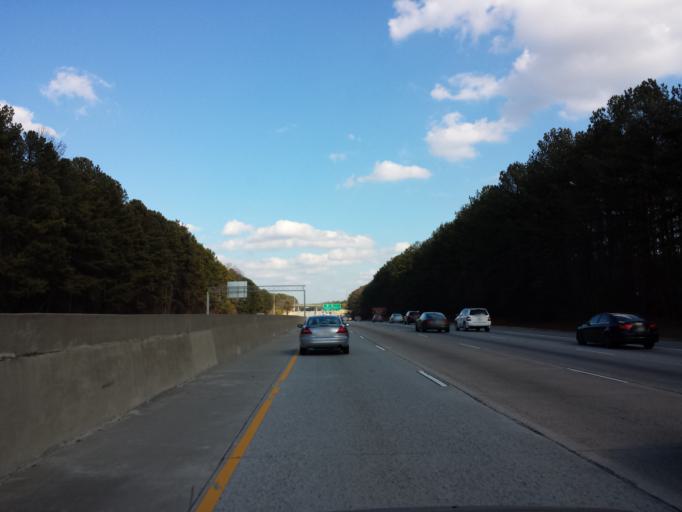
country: US
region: Georgia
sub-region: Fulton County
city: Alpharetta
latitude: 34.0516
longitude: -84.2953
